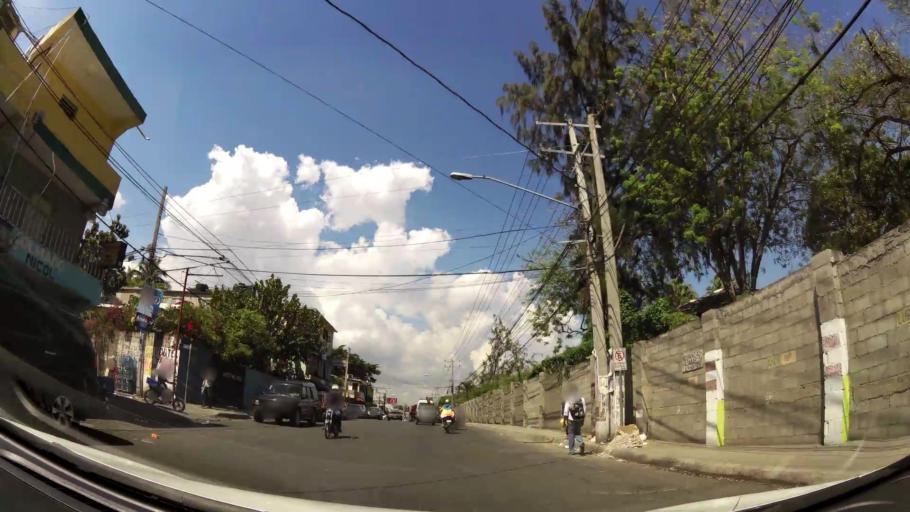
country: DO
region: Nacional
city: Bella Vista
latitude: 18.4535
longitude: -69.9782
